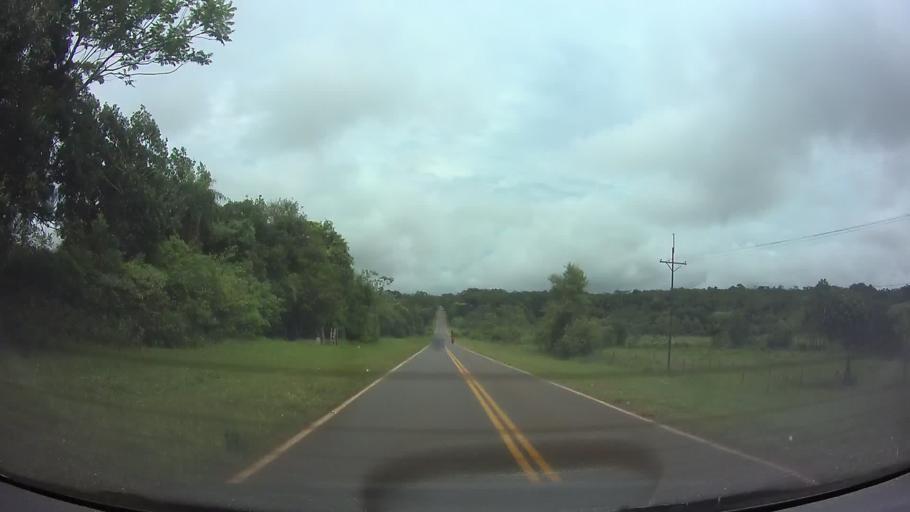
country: PY
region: Paraguari
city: Ybycui
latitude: -25.9725
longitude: -57.0770
